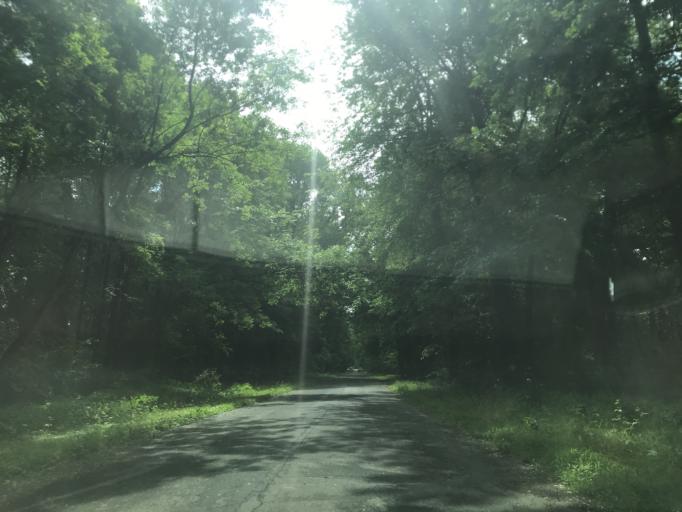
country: US
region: Maryland
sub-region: Caroline County
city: Ridgely
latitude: 38.9206
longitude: -75.9691
